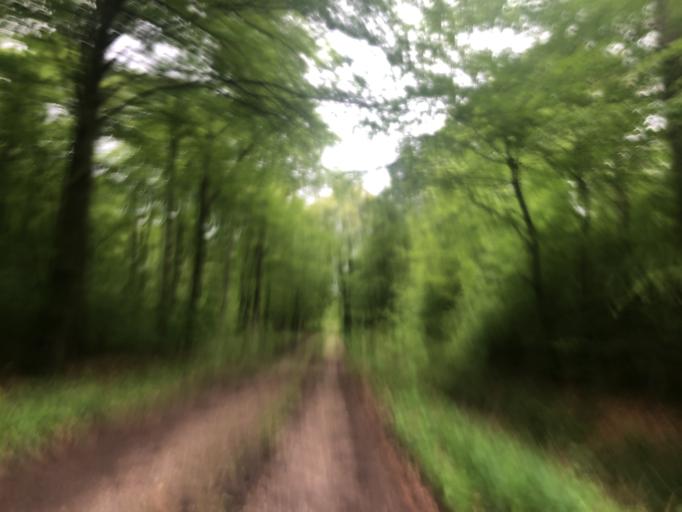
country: DK
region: Zealand
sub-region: Koge Kommune
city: Ejby
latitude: 55.4360
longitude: 12.0854
